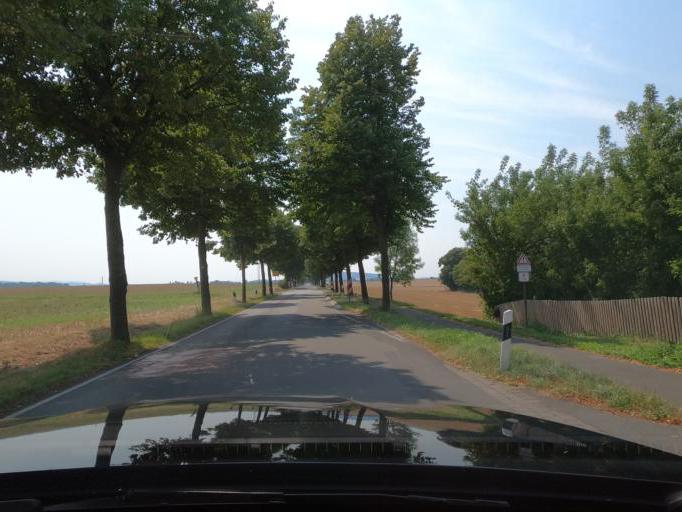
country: DE
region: Lower Saxony
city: Nordstemmen
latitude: 52.2125
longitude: 9.7927
